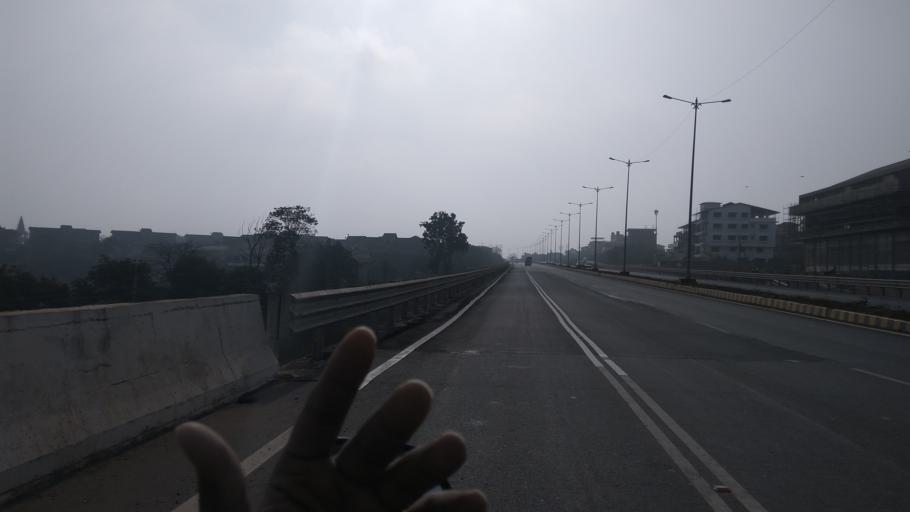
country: IN
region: Goa
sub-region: North Goa
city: Bambolim
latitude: 15.4968
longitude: 73.8788
